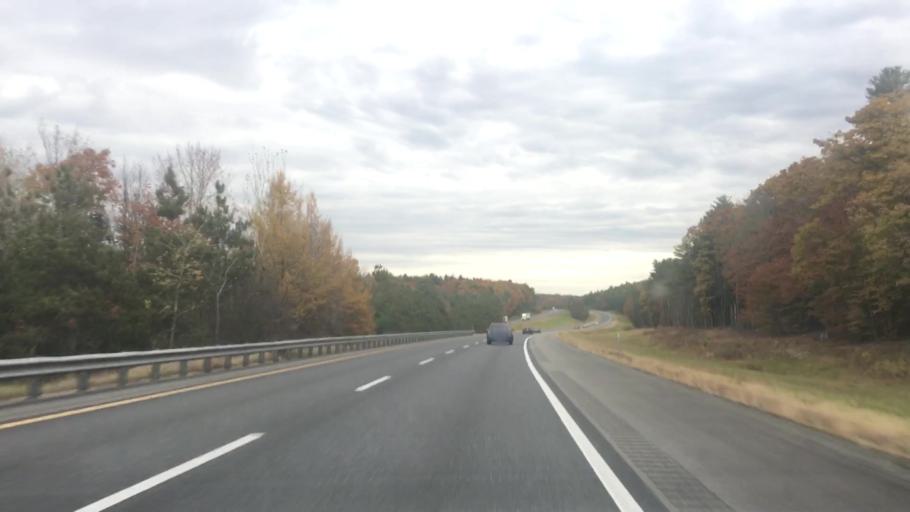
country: US
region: Maine
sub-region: Sagadahoc County
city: Topsham
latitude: 43.9787
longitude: -69.9446
